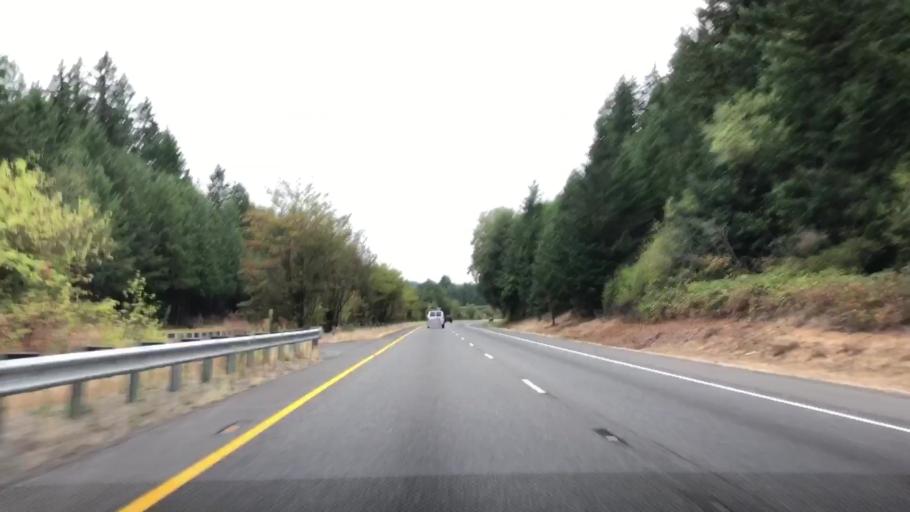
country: US
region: Washington
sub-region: Pierce County
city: Purdy
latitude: 47.3986
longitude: -122.6223
